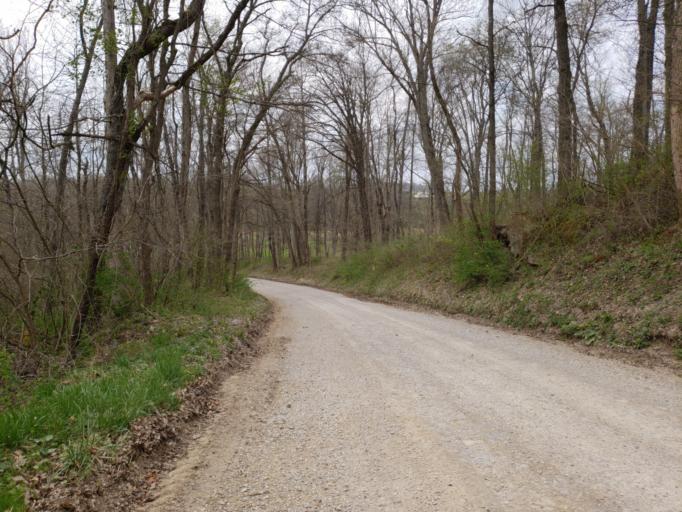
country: US
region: Ohio
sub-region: Tuscarawas County
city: Rockford
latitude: 40.4822
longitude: -81.2497
